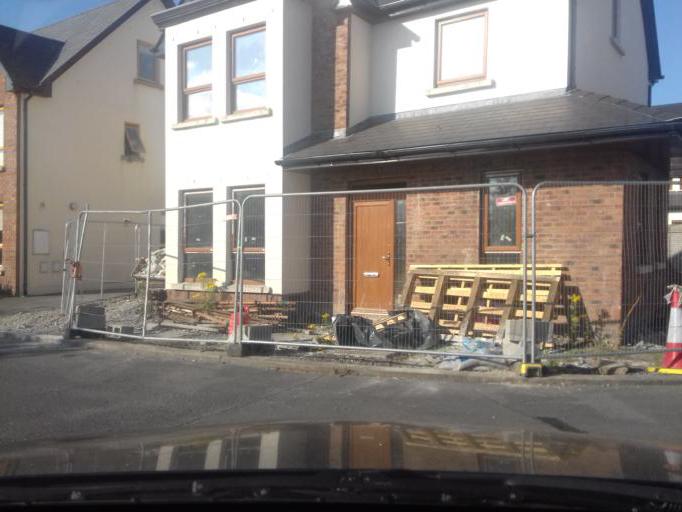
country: IE
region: Leinster
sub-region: Fingal County
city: Blanchardstown
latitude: 53.4337
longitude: -6.3774
